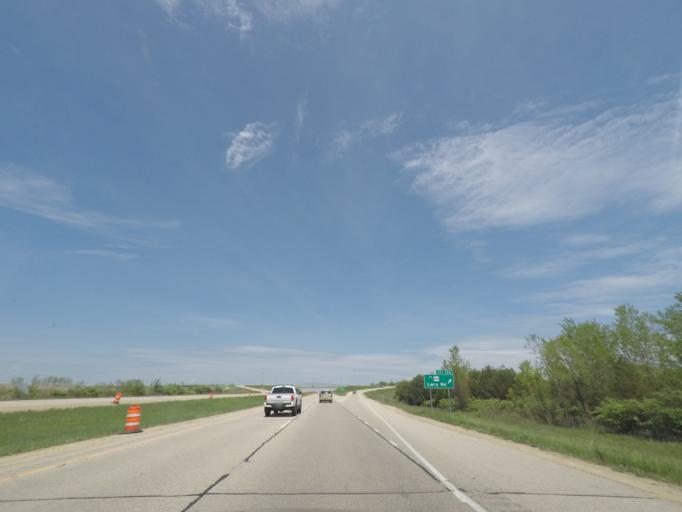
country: US
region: Wisconsin
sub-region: Dane County
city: Madison
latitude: 43.0054
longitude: -89.3836
